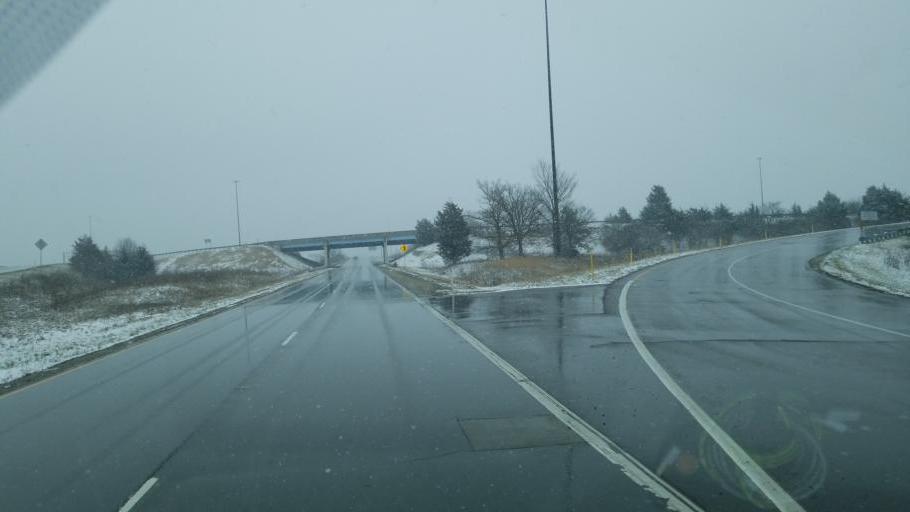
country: US
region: Indiana
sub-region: Wayne County
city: Richmond
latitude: 39.8697
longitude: -84.9299
